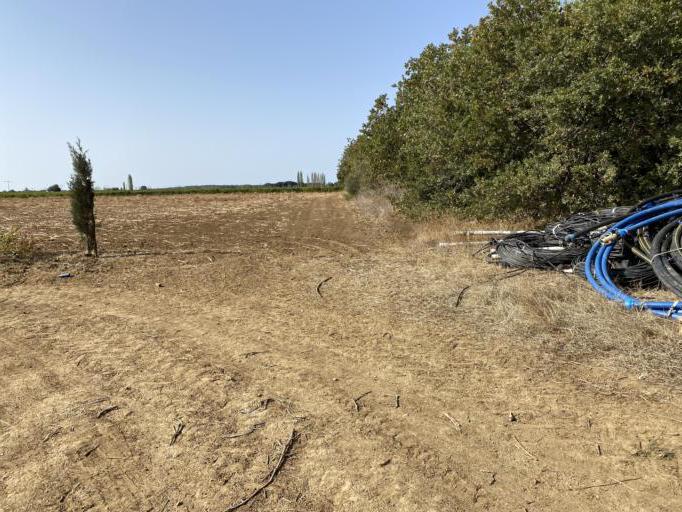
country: TR
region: Canakkale
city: Eceabat
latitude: 40.1807
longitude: 26.2875
